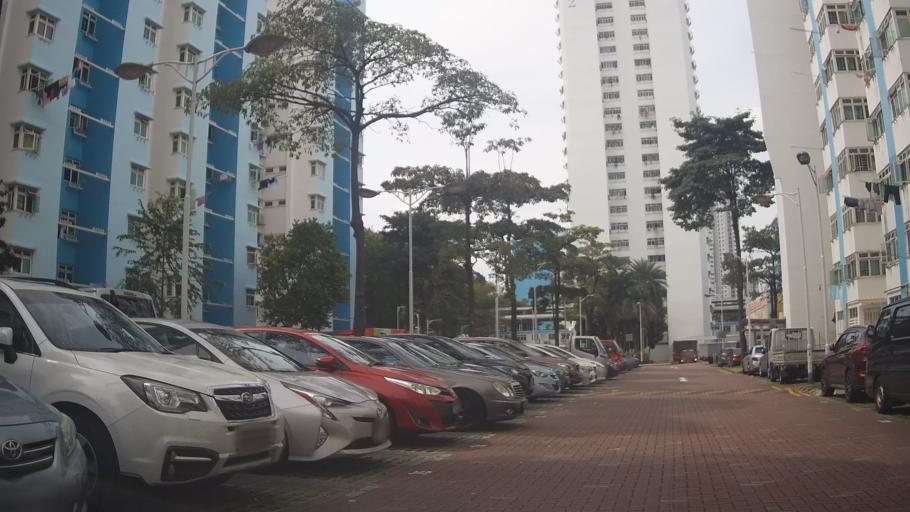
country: SG
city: Singapore
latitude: 1.3197
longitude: 103.8640
